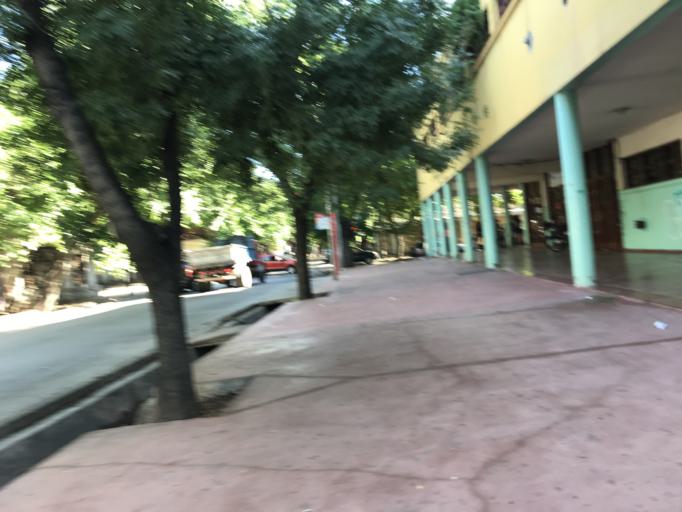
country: AR
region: Mendoza
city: Mendoza
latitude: -32.8805
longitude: -68.8309
